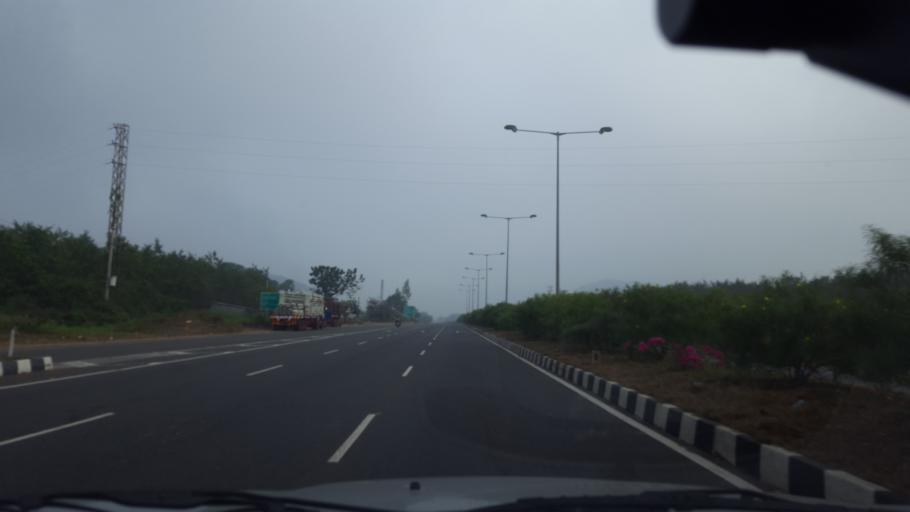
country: IN
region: Andhra Pradesh
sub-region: Prakasam
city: pedda nakkalapalem
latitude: 15.8709
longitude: 80.0644
